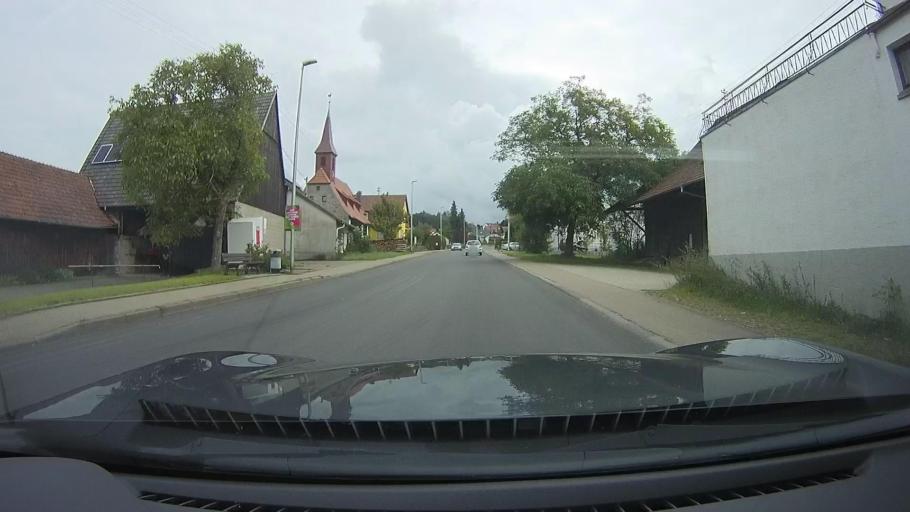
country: DE
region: Baden-Wuerttemberg
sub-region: Regierungsbezirk Stuttgart
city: Althutte
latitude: 48.9429
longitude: 9.5503
